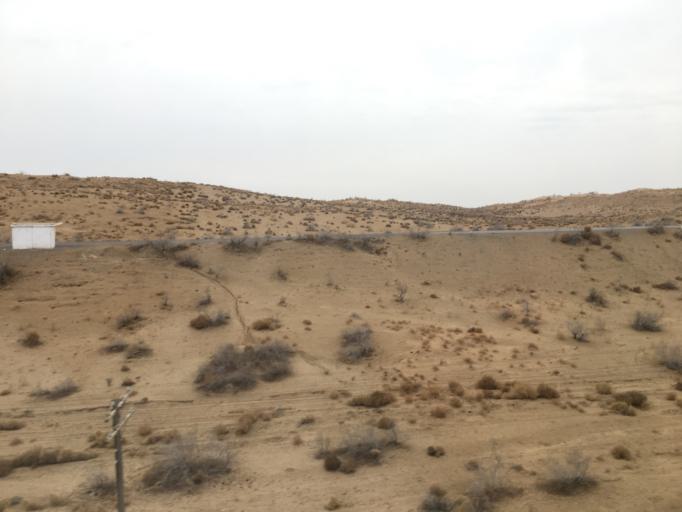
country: TM
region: Mary
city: Yoloeten
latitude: 36.4479
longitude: 62.5886
